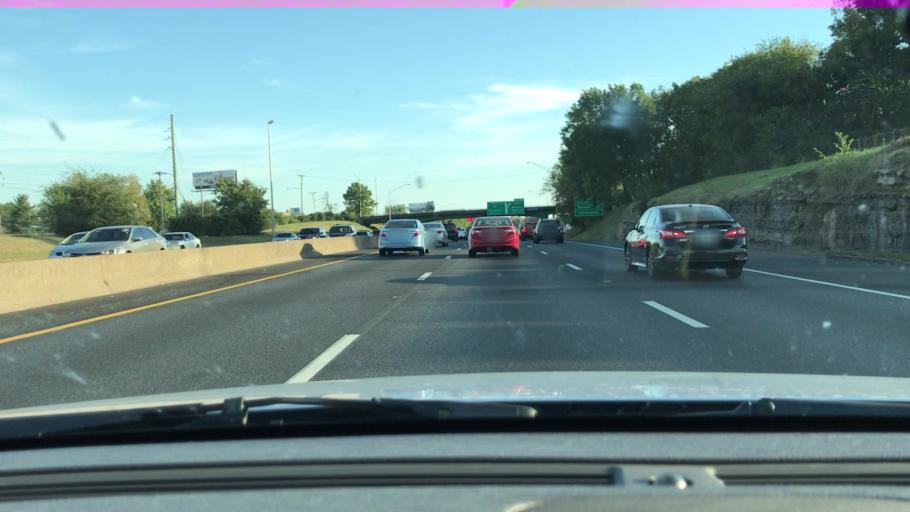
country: US
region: Tennessee
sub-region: Davidson County
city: Nashville
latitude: 36.1412
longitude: -86.7766
